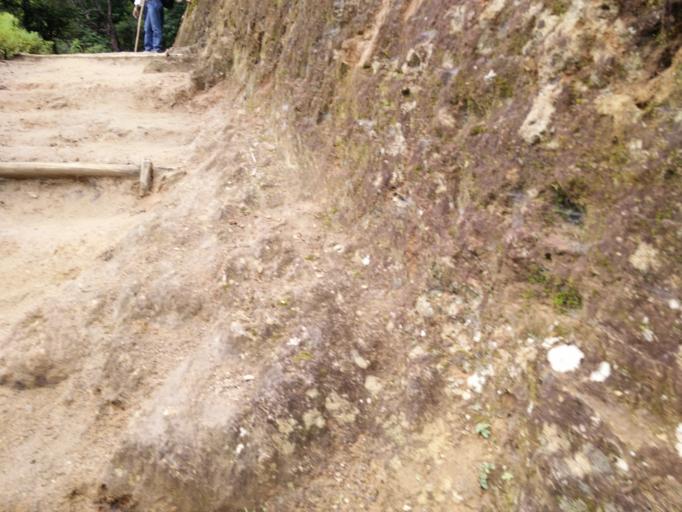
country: BT
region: Paro
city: Paro
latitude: 27.4856
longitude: 89.3607
